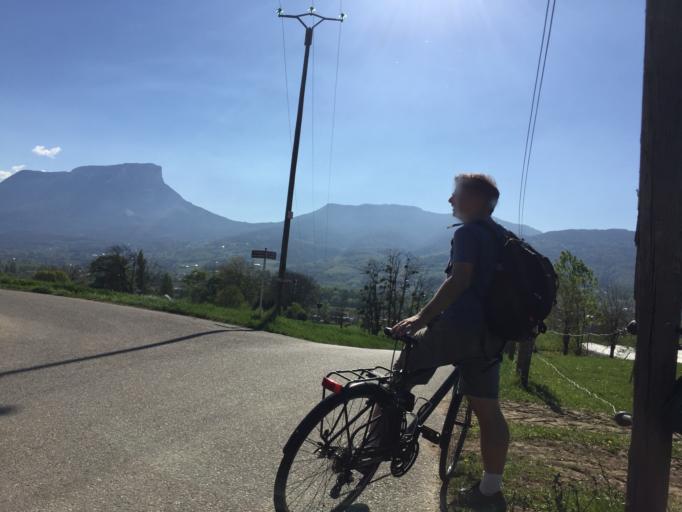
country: FR
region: Rhone-Alpes
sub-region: Departement de la Savoie
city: Challes-les-Eaux
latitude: 45.5283
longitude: 5.9822
